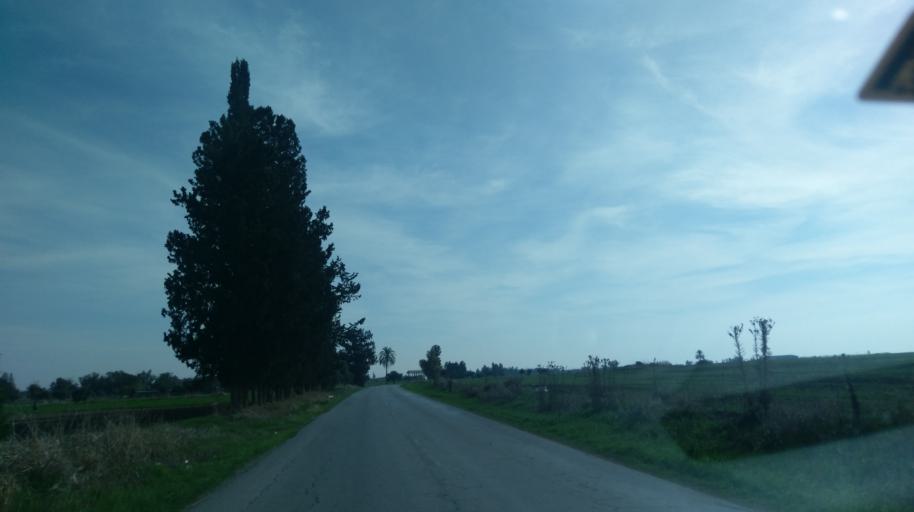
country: CY
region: Larnaka
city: Troulloi
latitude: 35.1556
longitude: 33.6230
